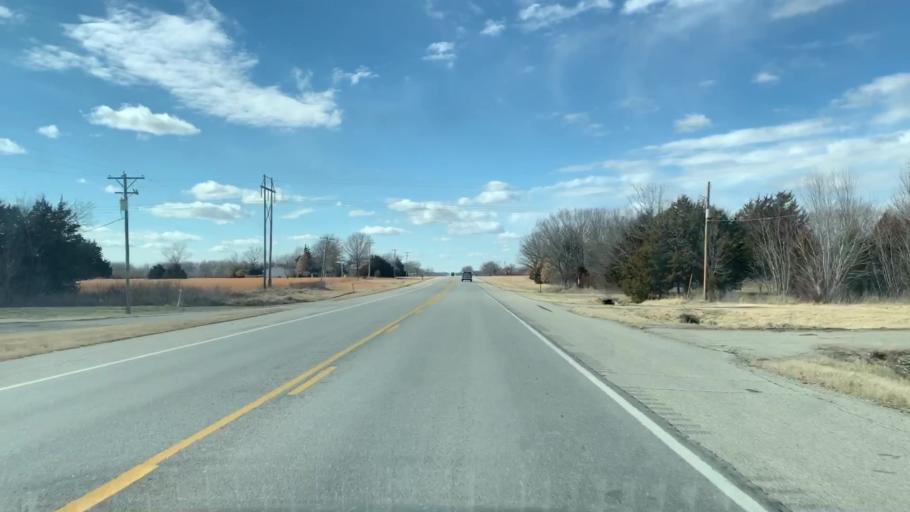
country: US
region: Kansas
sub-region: Labette County
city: Oswego
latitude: 37.3403
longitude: -95.0863
